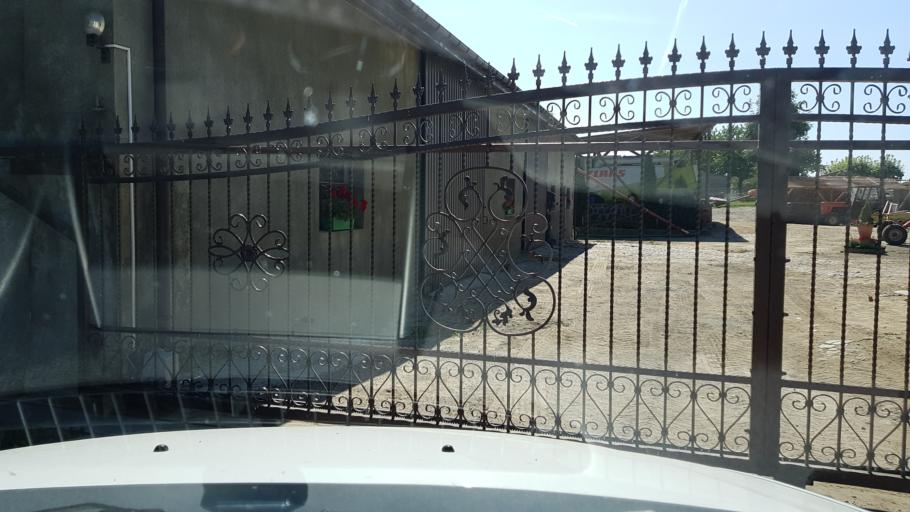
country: PL
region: West Pomeranian Voivodeship
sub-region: Powiat gryfinski
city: Moryn
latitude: 52.8744
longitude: 14.3078
